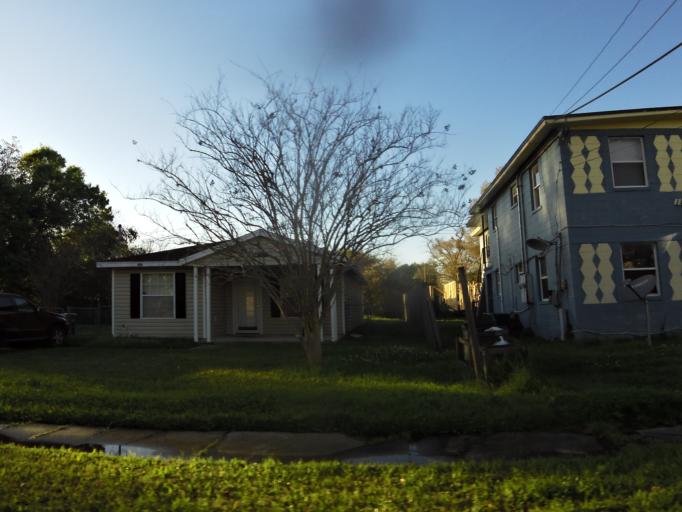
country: US
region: Florida
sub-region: Duval County
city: Jacksonville
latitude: 30.3356
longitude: -81.6902
